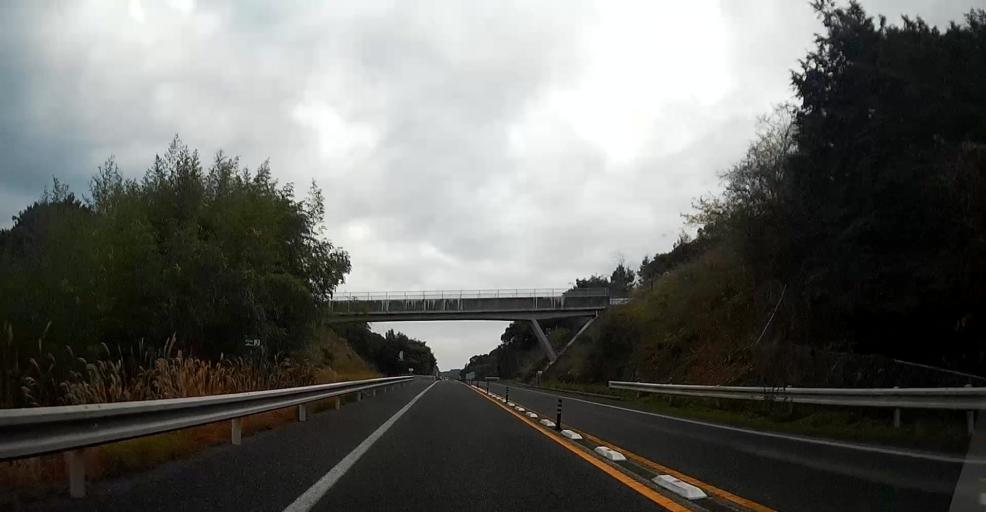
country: JP
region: Kumamoto
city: Hondo
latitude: 32.5092
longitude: 130.3493
